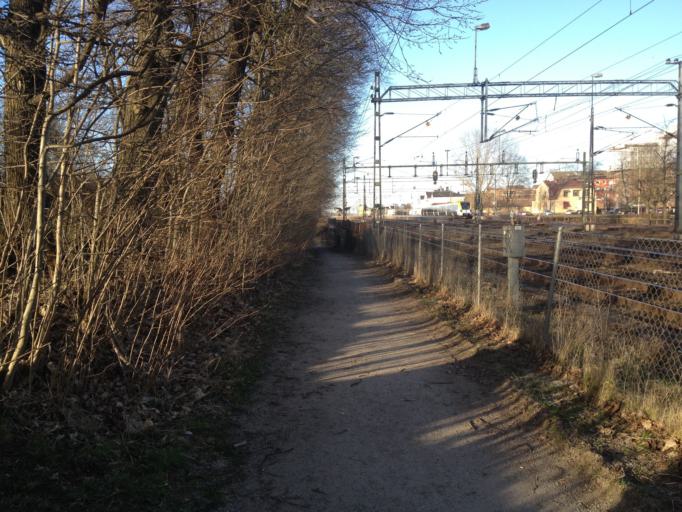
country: SE
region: Vaestra Goetaland
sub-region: Falkopings Kommun
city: Falkoeping
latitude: 58.1732
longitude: 13.5484
